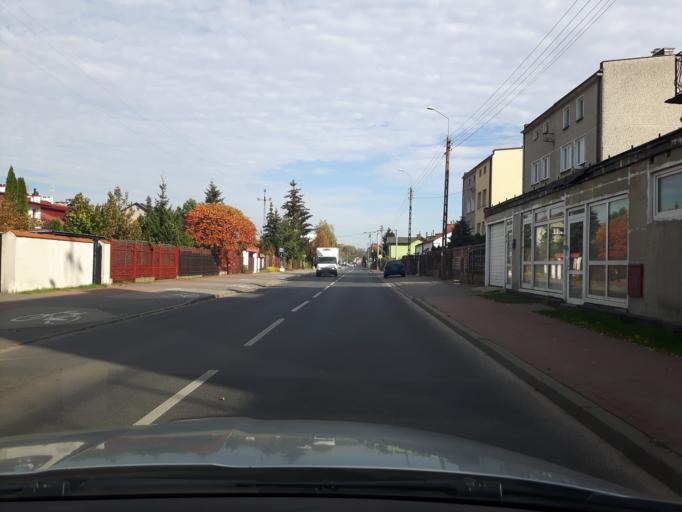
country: PL
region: Masovian Voivodeship
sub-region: Powiat wolominski
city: Zabki
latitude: 52.2970
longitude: 21.0980
